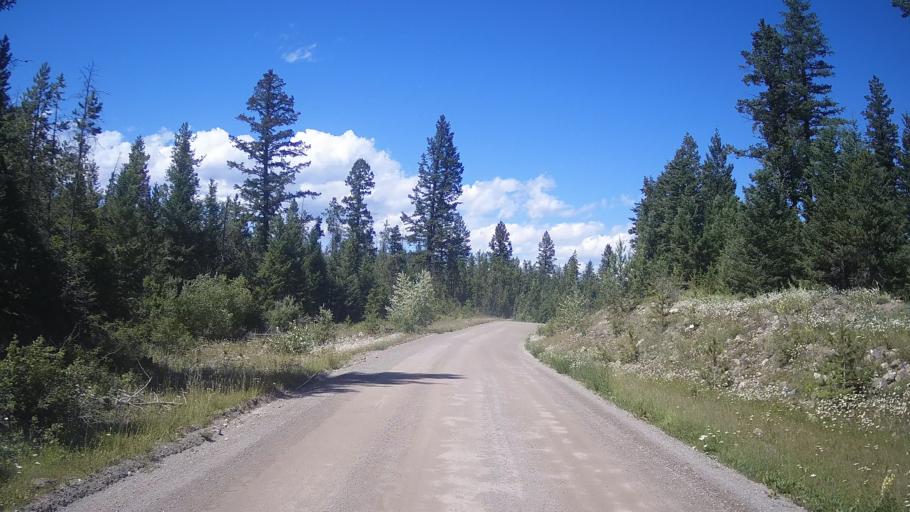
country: CA
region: British Columbia
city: Cache Creek
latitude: 51.1650
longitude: -121.5611
